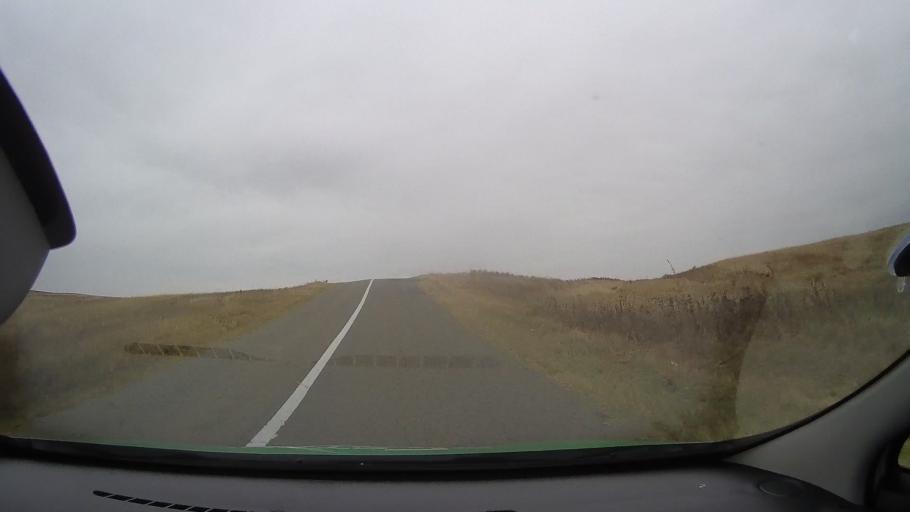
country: RO
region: Constanta
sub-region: Comuna Saraiu
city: Saraiu
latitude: 44.7253
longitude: 28.1831
